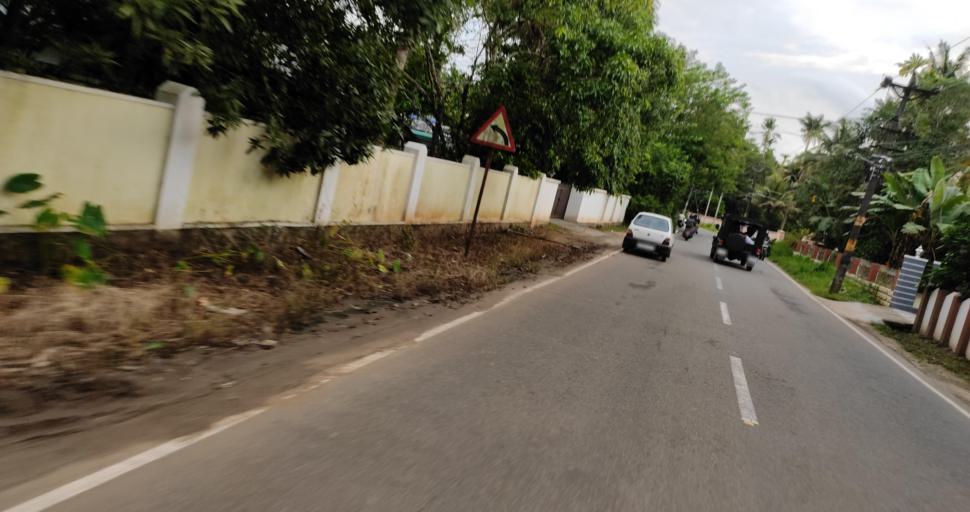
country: IN
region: Kerala
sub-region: Thrissur District
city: Kizhake Chalakudi
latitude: 10.3179
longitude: 76.3564
